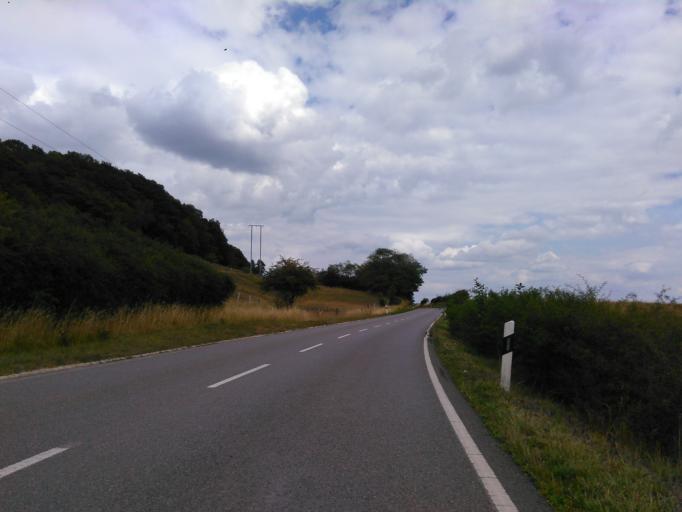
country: LU
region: Grevenmacher
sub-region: Canton de Grevenmacher
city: Junglinster
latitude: 49.6999
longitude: 6.2652
